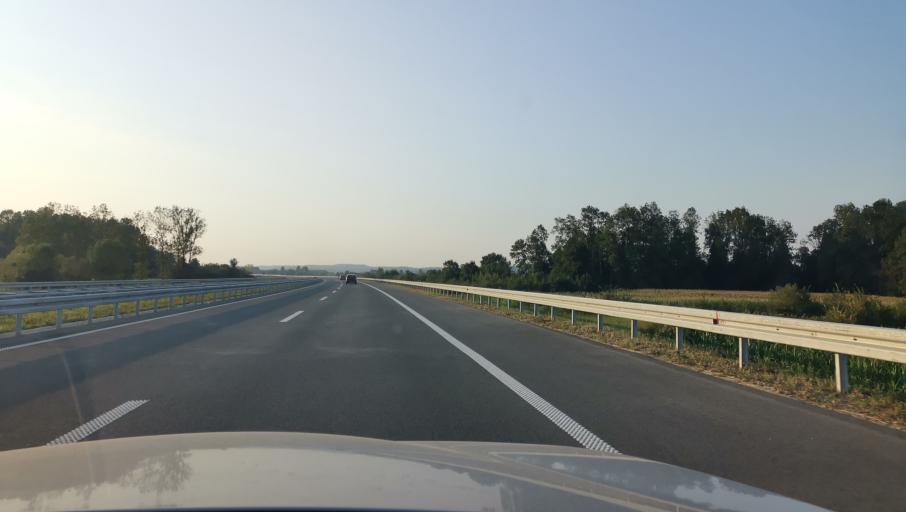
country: RS
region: Central Serbia
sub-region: Kolubarski Okrug
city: Ljig
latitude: 44.2710
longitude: 20.2683
